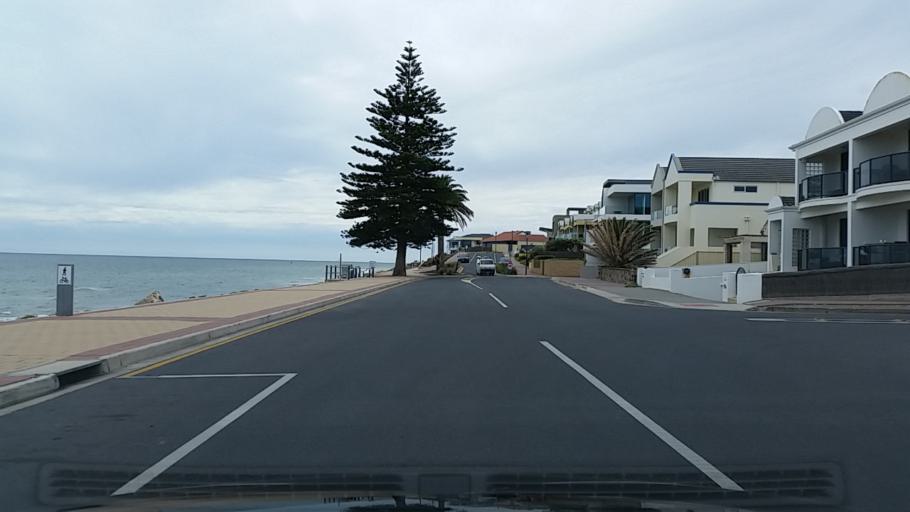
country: AU
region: South Australia
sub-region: Holdfast Bay
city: North Brighton
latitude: -35.0100
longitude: 138.5125
